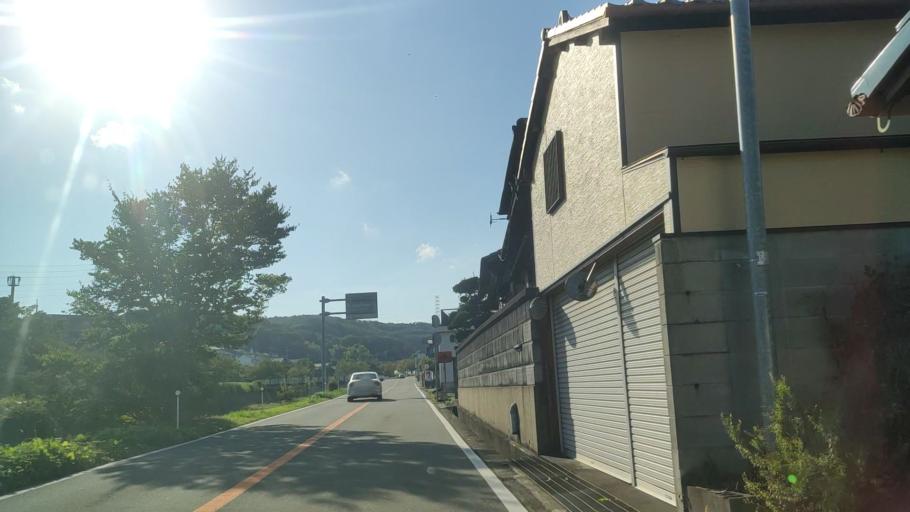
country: JP
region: Hyogo
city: Sandacho
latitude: 34.8244
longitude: 135.2445
